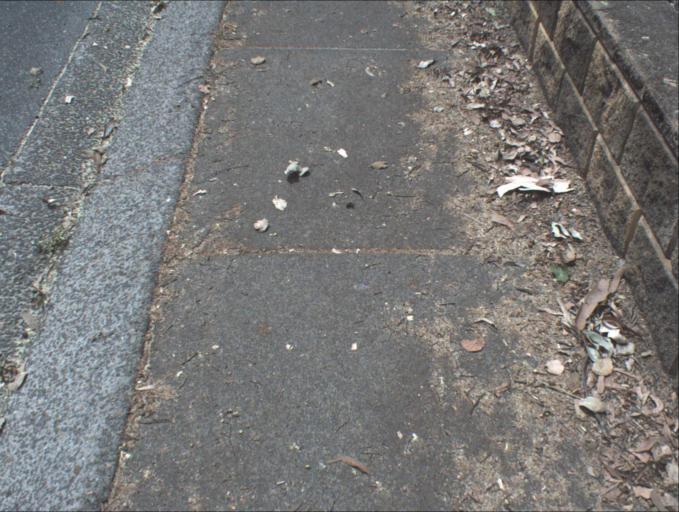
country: AU
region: Queensland
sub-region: Logan
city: Beenleigh
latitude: -27.7148
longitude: 153.1980
